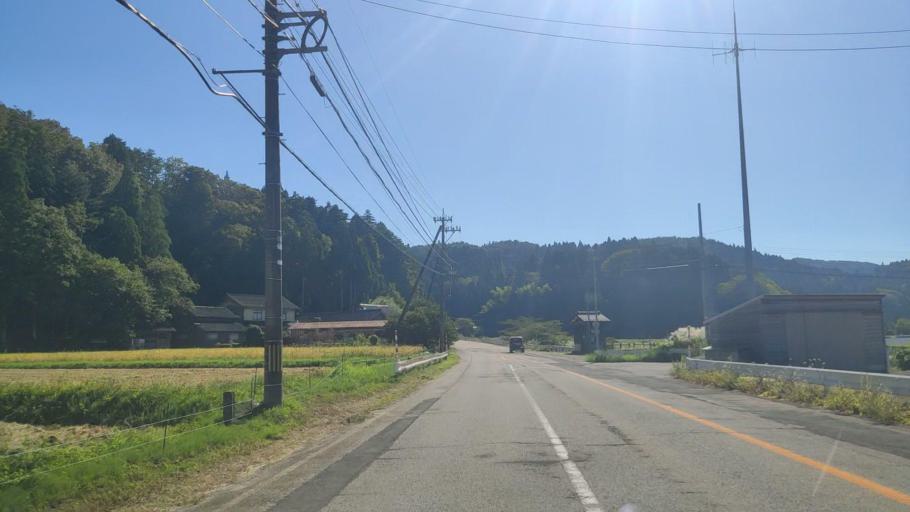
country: JP
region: Ishikawa
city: Nanao
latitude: 37.3356
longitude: 137.2091
